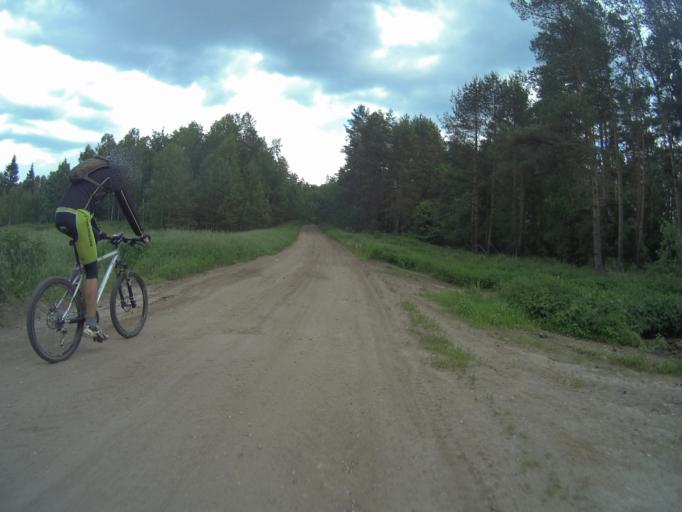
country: RU
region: Vladimir
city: Raduzhnyy
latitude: 56.0047
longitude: 40.2064
